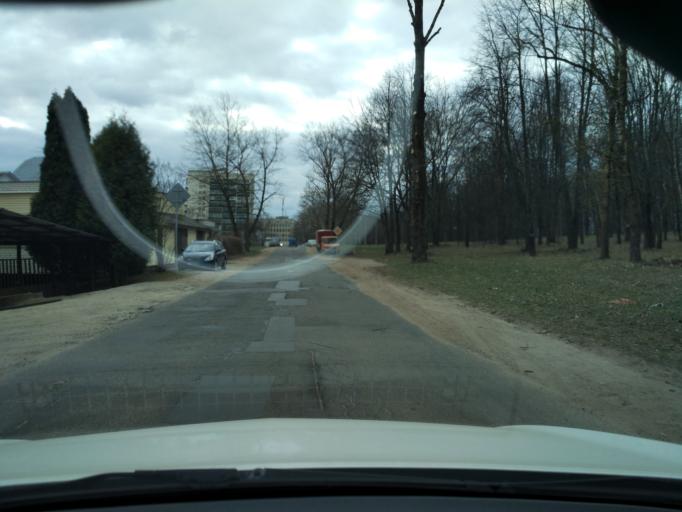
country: BY
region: Minsk
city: Minsk
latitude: 53.9396
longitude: 27.5496
